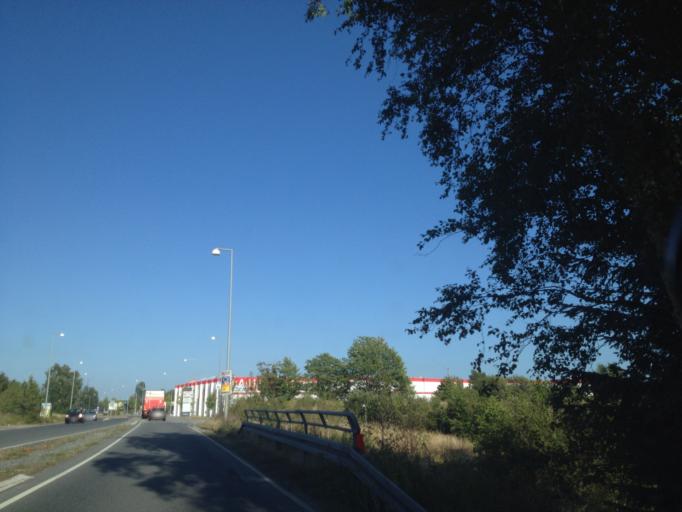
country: DK
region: Capital Region
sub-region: Hillerod Kommune
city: Hillerod
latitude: 55.9348
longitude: 12.2559
